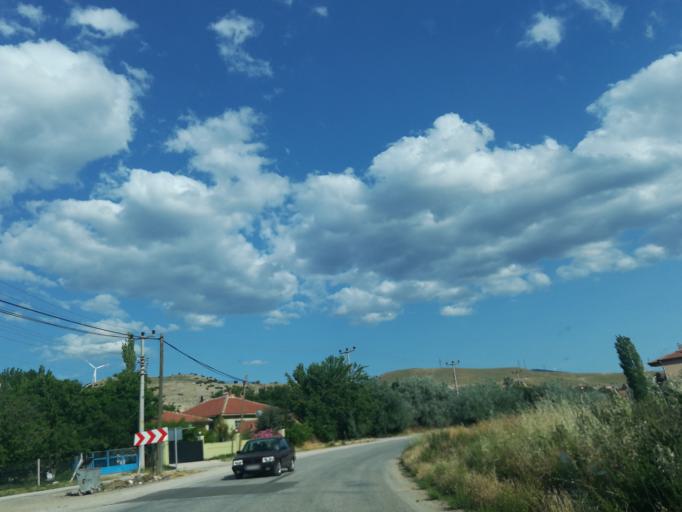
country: TR
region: Afyonkarahisar
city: Dinar
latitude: 38.0823
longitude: 30.1667
